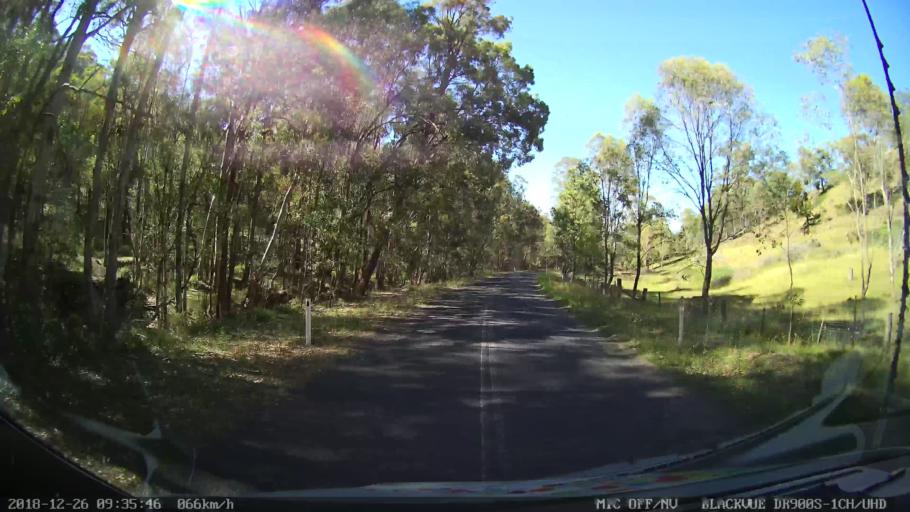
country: AU
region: New South Wales
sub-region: Mid-Western Regional
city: Kandos
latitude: -32.9179
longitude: 150.0415
